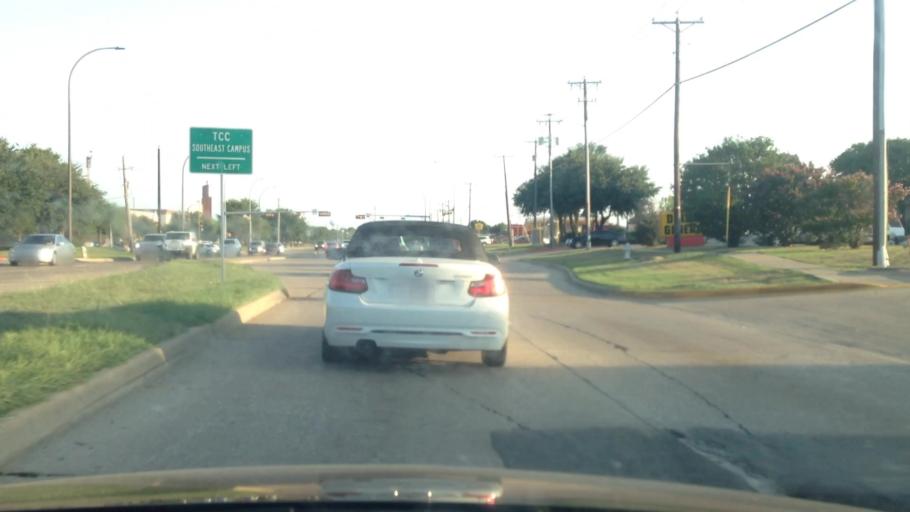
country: US
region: Texas
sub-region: Tarrant County
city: Dalworthington Gardens
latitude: 32.6610
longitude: -97.1151
